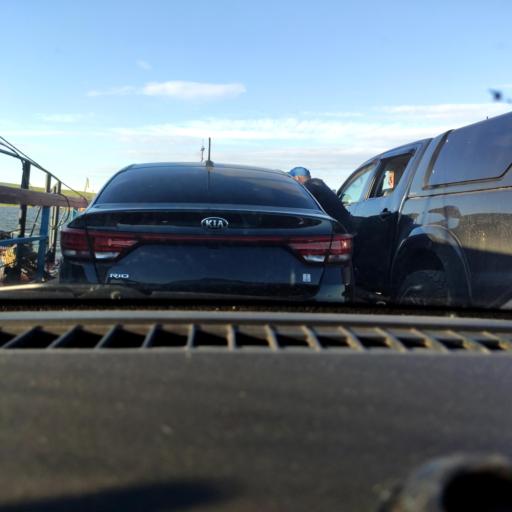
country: RU
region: Perm
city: Verkhnechusovskiye Gorodki
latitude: 58.1888
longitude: 57.1241
